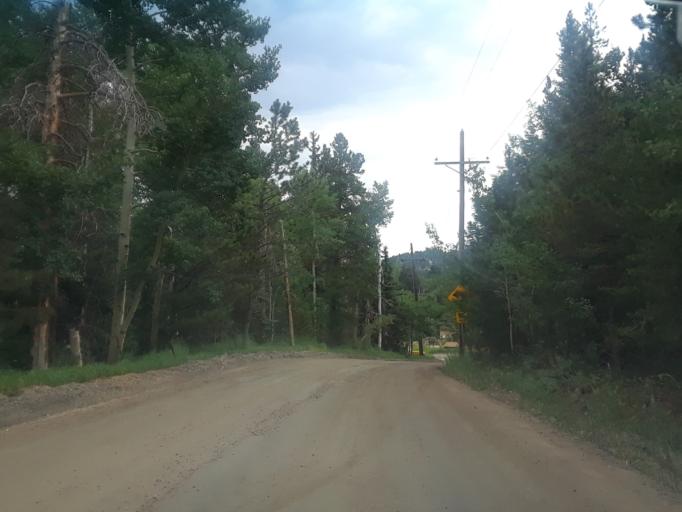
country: US
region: Colorado
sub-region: Boulder County
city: Nederland
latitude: 40.0618
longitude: -105.4142
